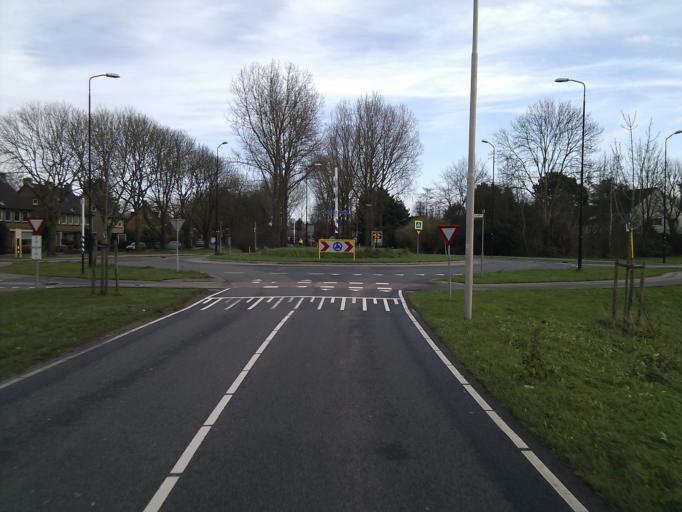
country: NL
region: North Holland
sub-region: Gemeente Amsterdam
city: Amsterdam-Zuidoost
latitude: 52.2674
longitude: 4.9667
